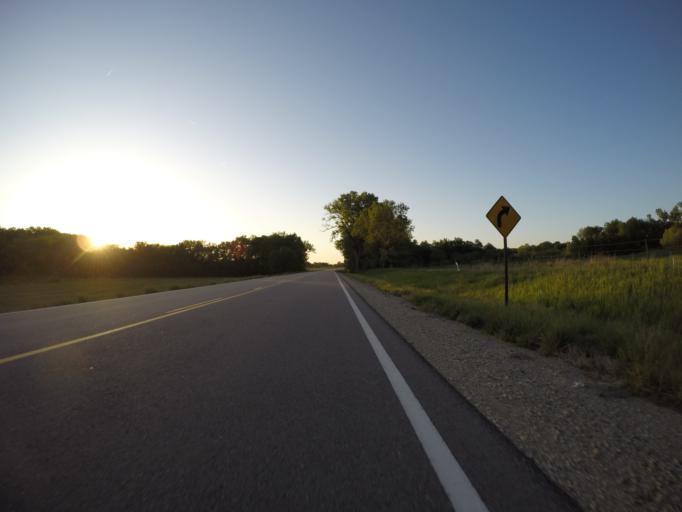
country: US
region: Kansas
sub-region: Riley County
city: Fort Riley North
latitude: 39.2558
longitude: -96.7737
